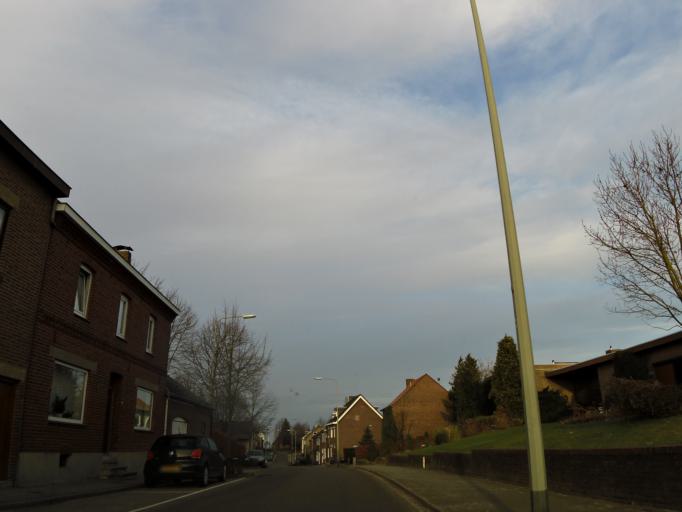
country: NL
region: Limburg
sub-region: Gemeente Simpelveld
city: Simpelveld
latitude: 50.8439
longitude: 5.9718
